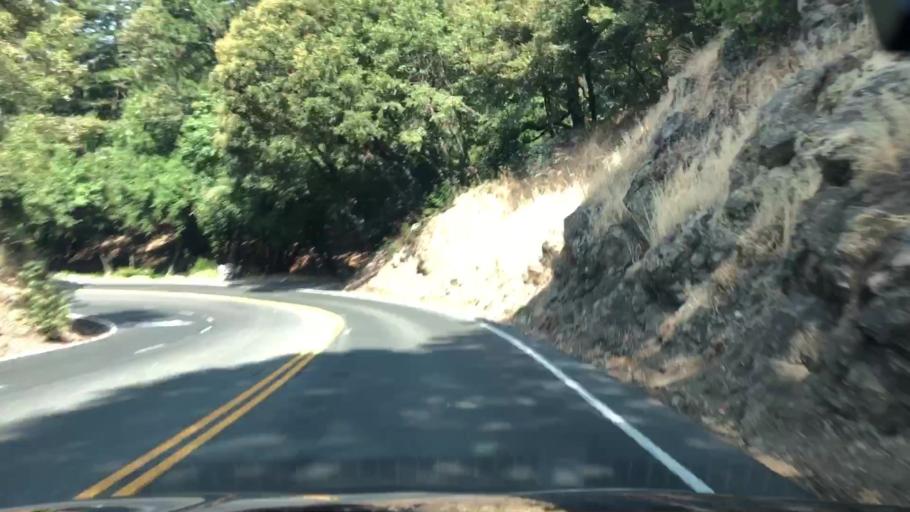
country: US
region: California
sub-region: Napa County
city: Calistoga
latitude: 38.6457
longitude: -122.5915
